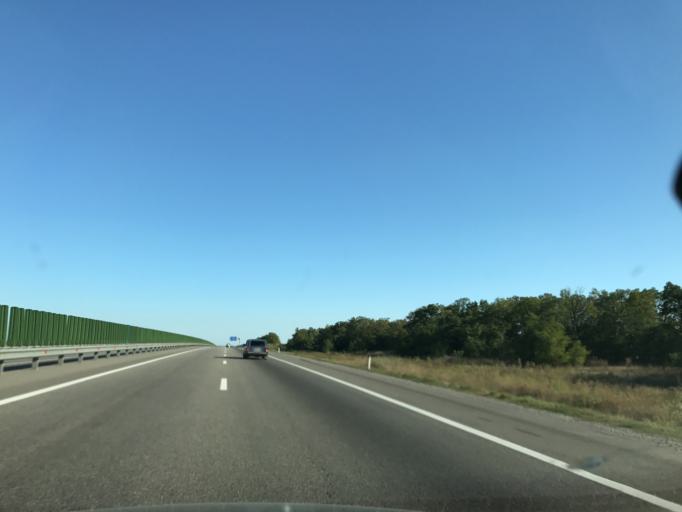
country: RU
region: Rostov
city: Glubokiy
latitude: 48.5769
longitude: 40.3519
